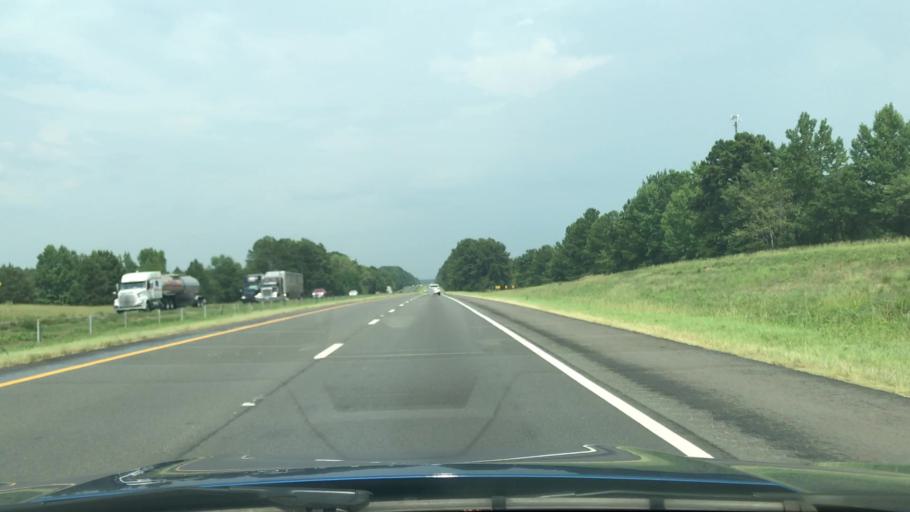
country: US
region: Texas
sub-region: Harrison County
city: Hallsville
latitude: 32.4761
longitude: -94.5662
